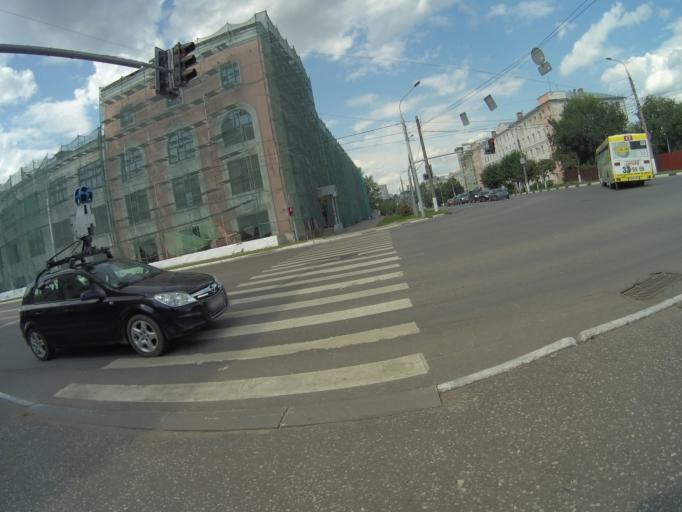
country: RU
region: Vladimir
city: Vladimir
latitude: 56.1282
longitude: 40.3935
